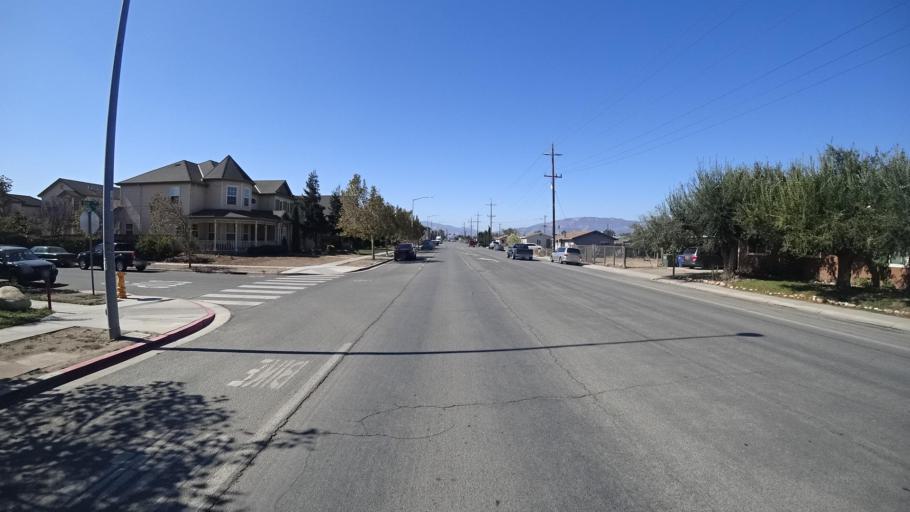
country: US
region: California
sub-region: Monterey County
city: Greenfield
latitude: 36.3193
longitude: -121.2378
